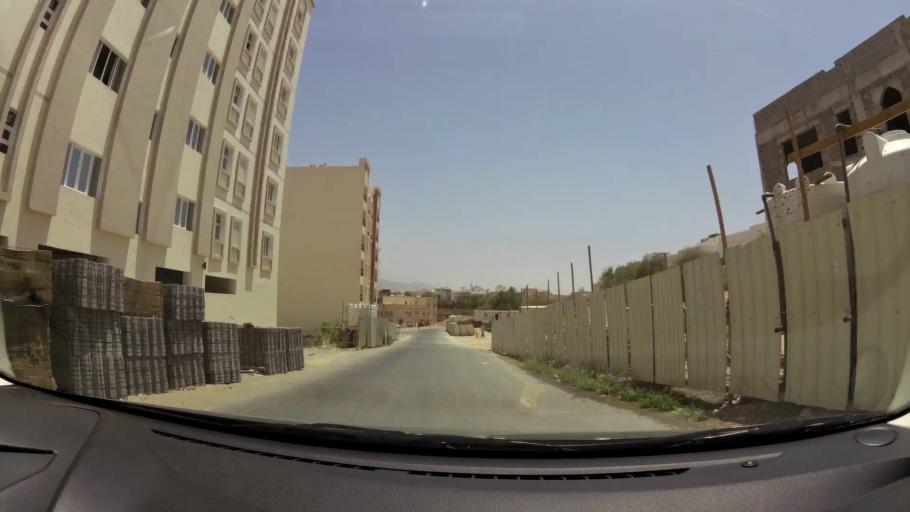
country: OM
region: Muhafazat Masqat
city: Muscat
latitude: 23.6225
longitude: 58.5012
